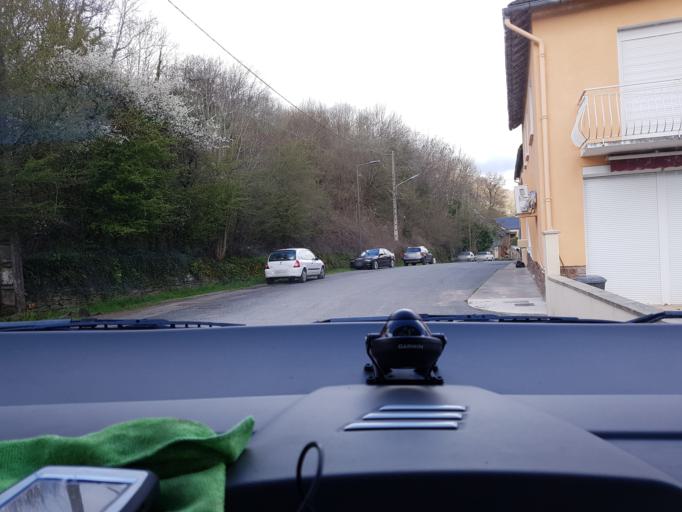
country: FR
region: Midi-Pyrenees
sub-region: Departement de l'Aveyron
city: Moyrazes
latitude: 44.3766
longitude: 2.4434
